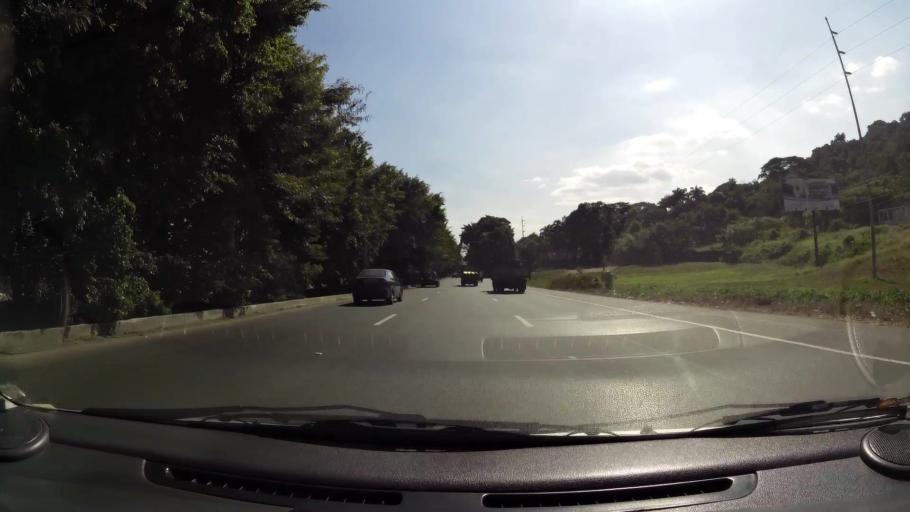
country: EC
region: Guayas
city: Santa Lucia
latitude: -2.1870
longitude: -79.9596
